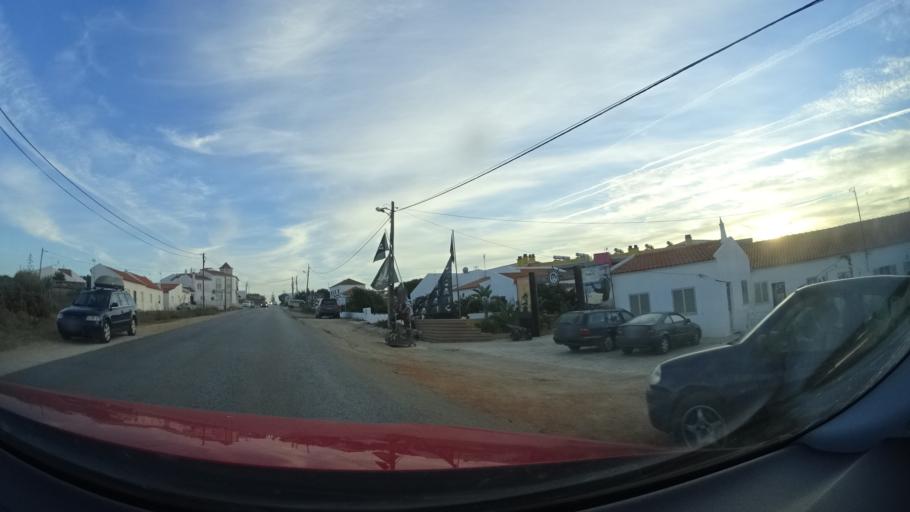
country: PT
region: Faro
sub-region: Vila do Bispo
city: Sagres
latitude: 37.0109
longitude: -8.9435
